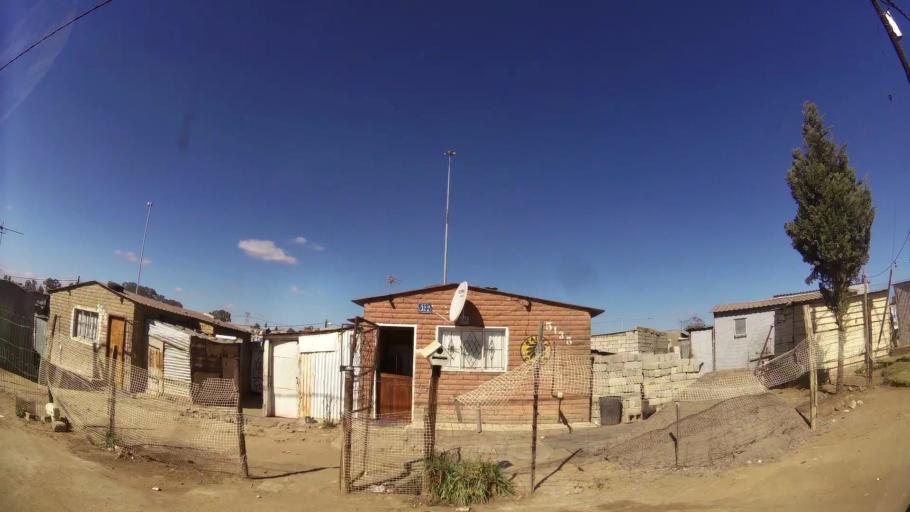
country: ZA
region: Gauteng
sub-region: City of Johannesburg Metropolitan Municipality
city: Midrand
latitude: -25.9215
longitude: 28.0938
